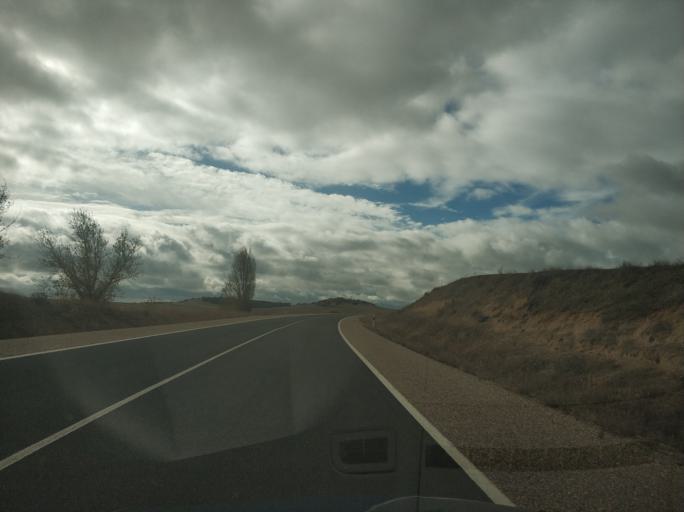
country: ES
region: Castille and Leon
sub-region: Provincia de Zamora
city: Castrillo de la Guarena
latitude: 41.2088
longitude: -5.3234
